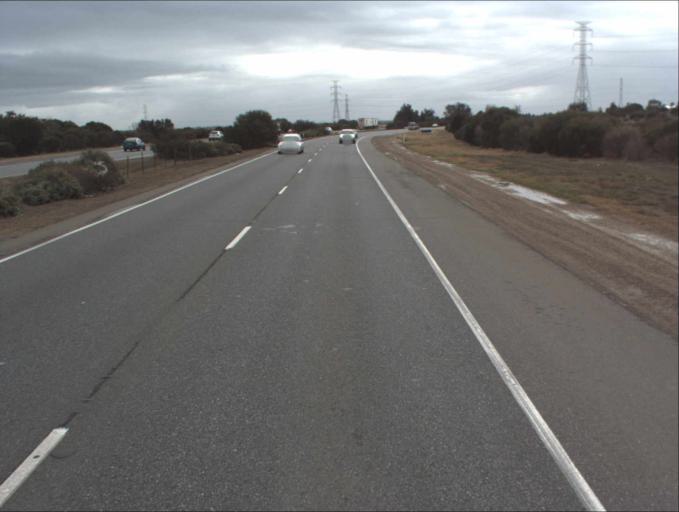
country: AU
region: South Australia
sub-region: Port Adelaide Enfield
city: Enfield
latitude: -34.8247
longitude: 138.5866
